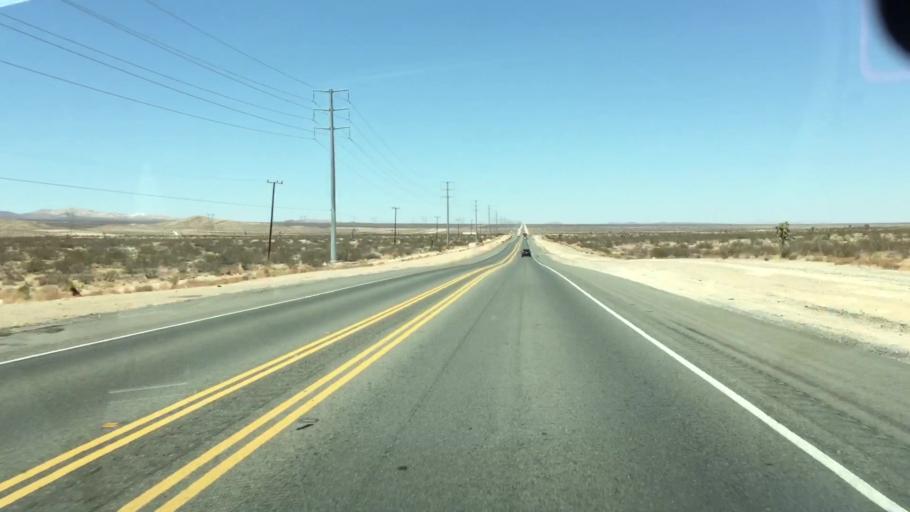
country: US
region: California
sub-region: San Bernardino County
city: Adelanto
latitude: 34.6385
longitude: -117.4324
